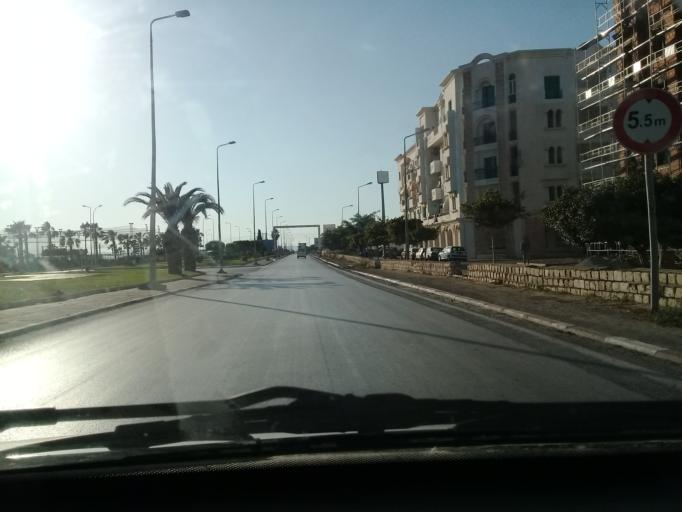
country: TN
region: Tunis
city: La Goulette
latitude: 36.8152
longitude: 10.3006
